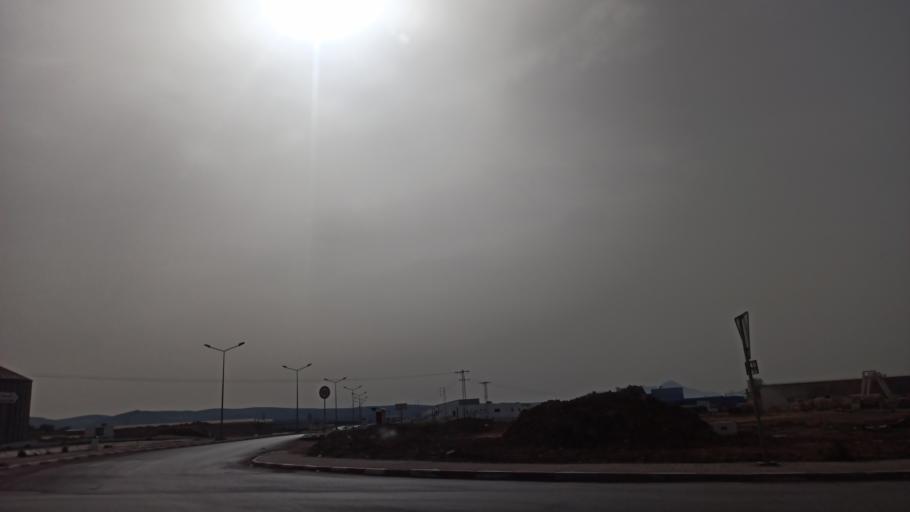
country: TN
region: Tunis
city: La Mohammedia
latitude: 36.5645
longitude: 10.0820
